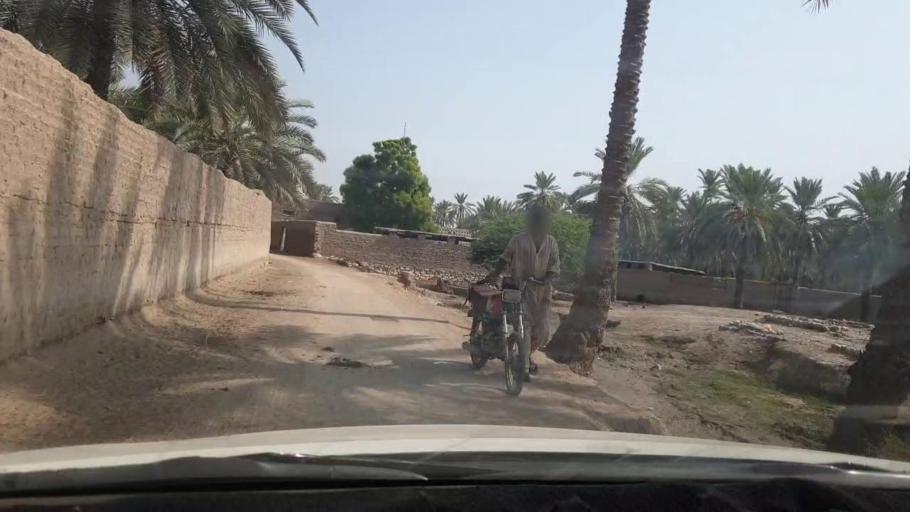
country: PK
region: Sindh
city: Rohri
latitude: 27.6020
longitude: 68.8908
